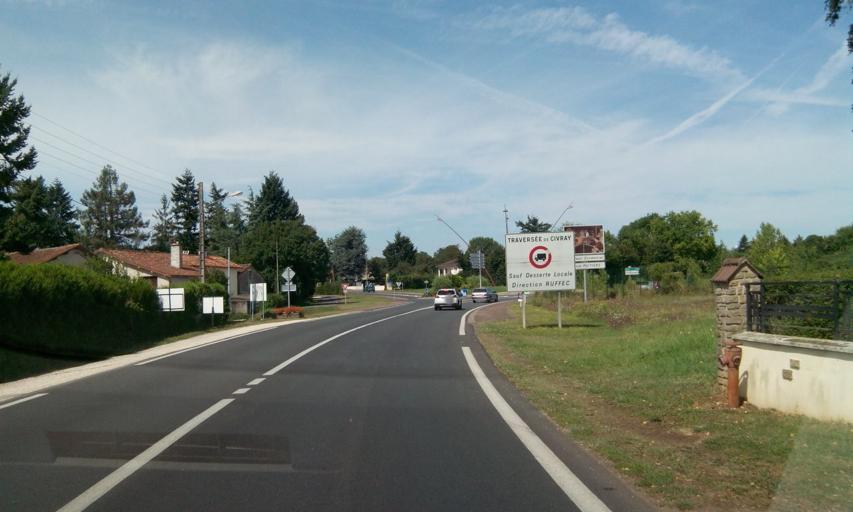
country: FR
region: Poitou-Charentes
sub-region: Departement de la Vienne
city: Savigne
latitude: 46.1595
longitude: 0.3041
